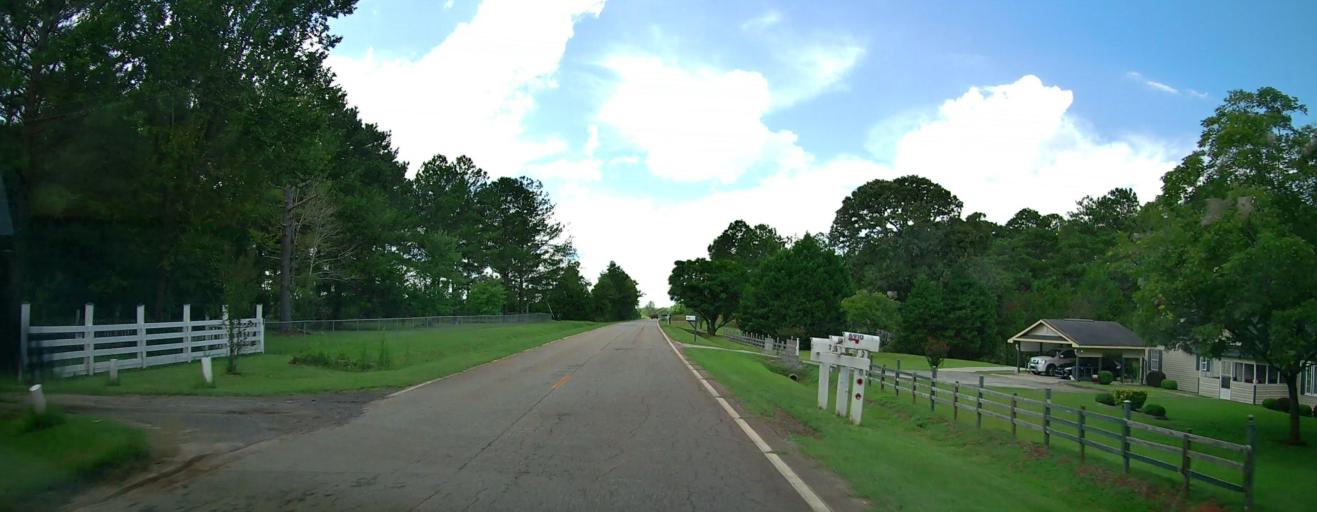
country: US
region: Georgia
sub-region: Houston County
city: Perry
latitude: 32.5221
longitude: -83.7579
